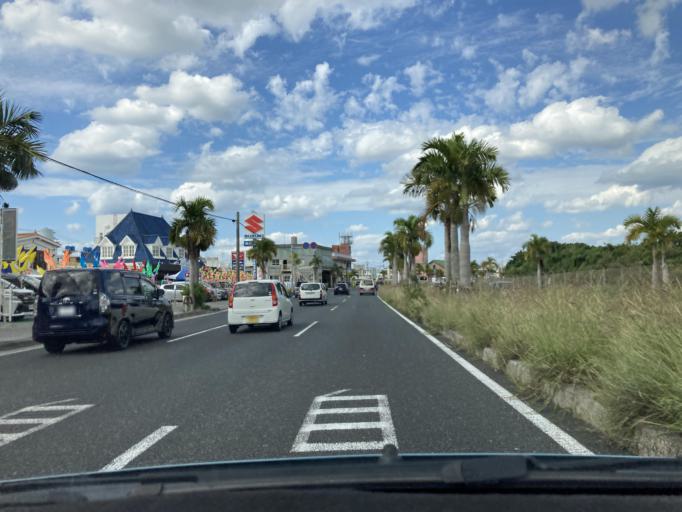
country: JP
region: Okinawa
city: Chatan
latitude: 26.3533
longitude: 127.7458
